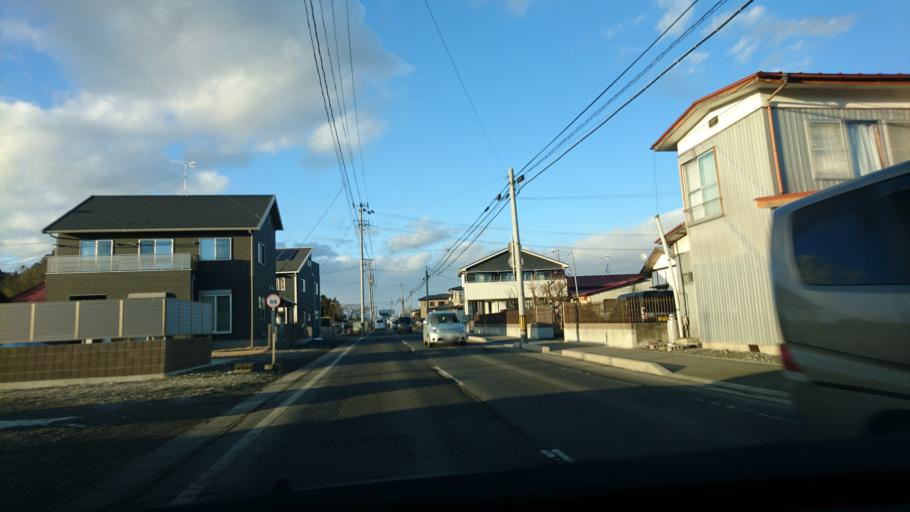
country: JP
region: Miyagi
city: Wakuya
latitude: 38.6985
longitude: 141.1917
